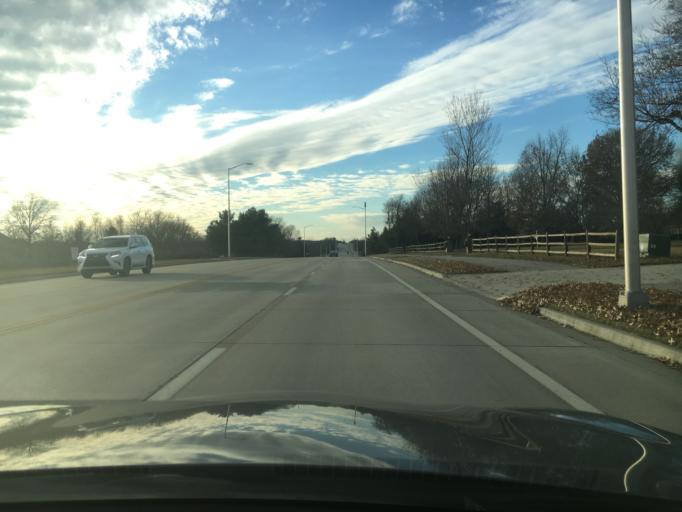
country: US
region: Kansas
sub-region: Johnson County
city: Leawood
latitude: 38.8693
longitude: -94.6334
